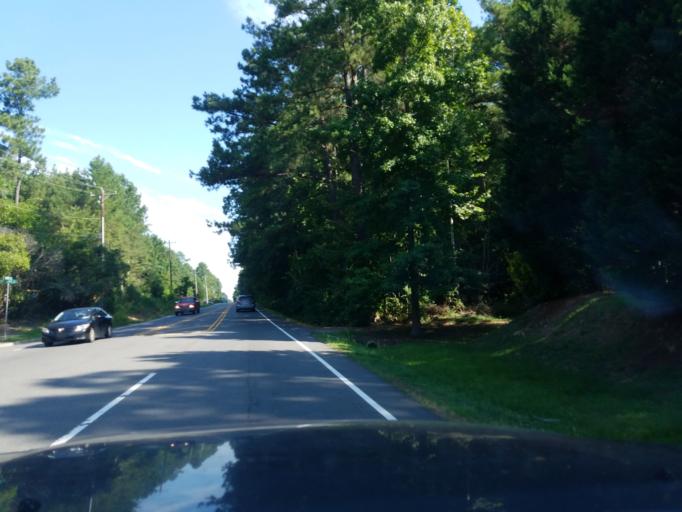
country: US
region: North Carolina
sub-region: Durham County
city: Durham
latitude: 35.9397
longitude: -78.9647
